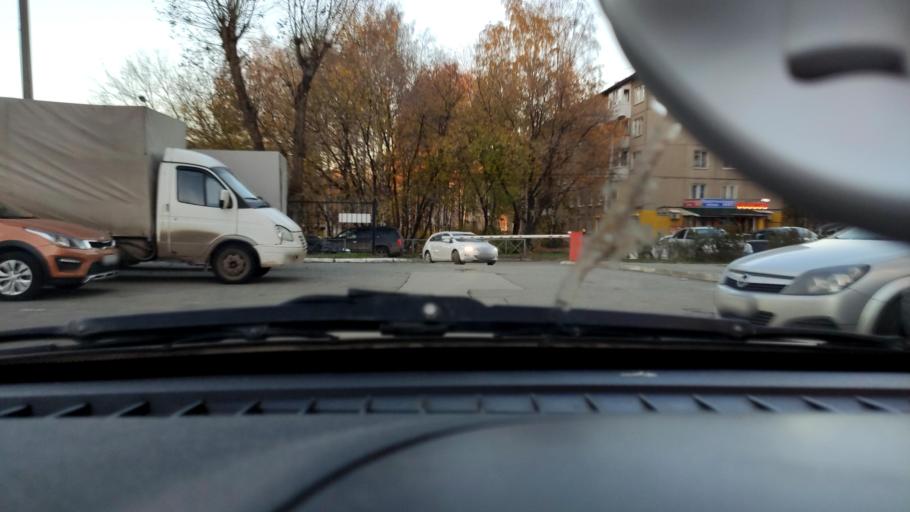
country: RU
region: Perm
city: Perm
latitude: 57.9833
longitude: 56.2174
